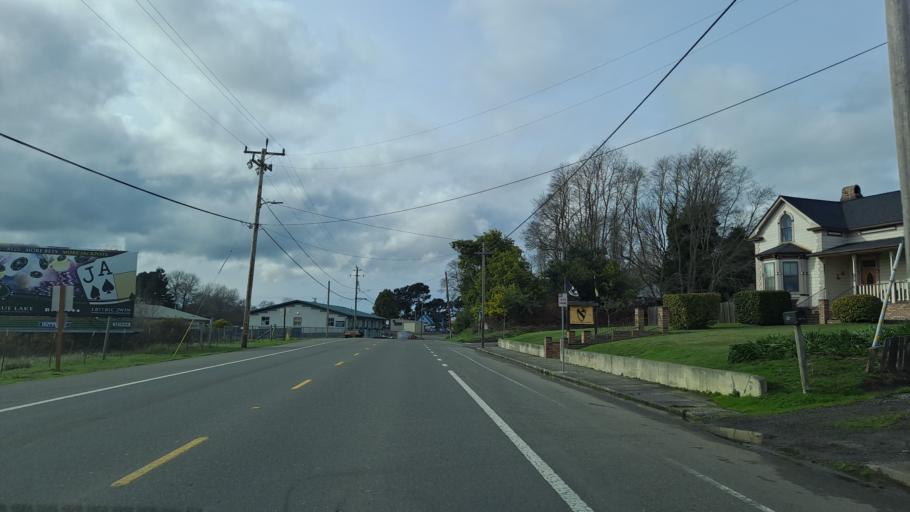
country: US
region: California
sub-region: Humboldt County
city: Fortuna
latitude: 40.5991
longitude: -124.1639
